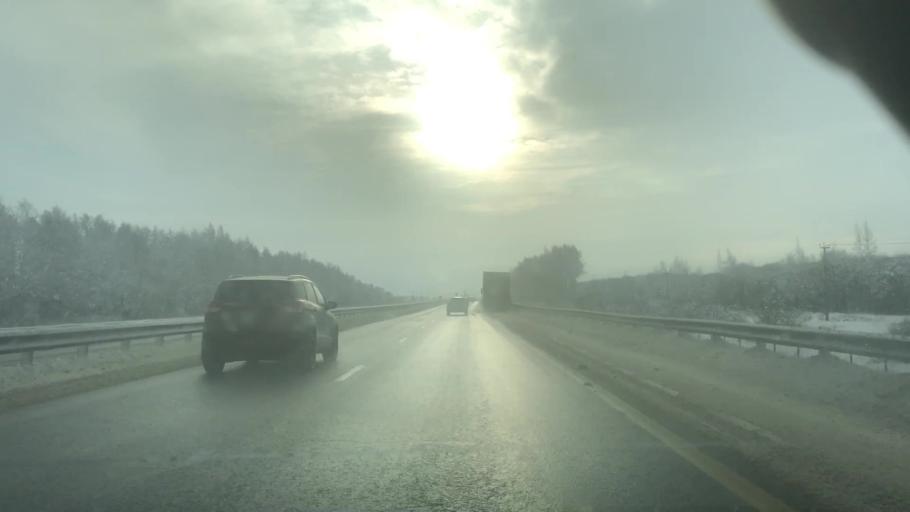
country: RU
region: Tula
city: Venev
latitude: 54.2868
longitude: 38.1588
